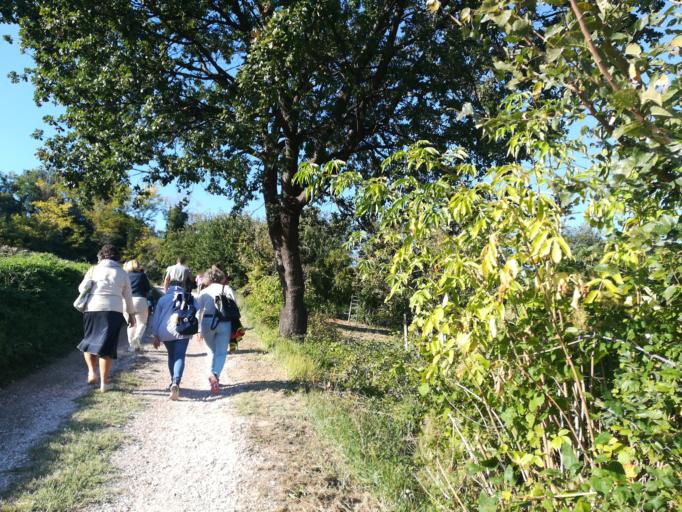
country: IT
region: The Marches
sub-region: Provincia di Macerata
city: Macerata
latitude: 43.3055
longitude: 13.4544
